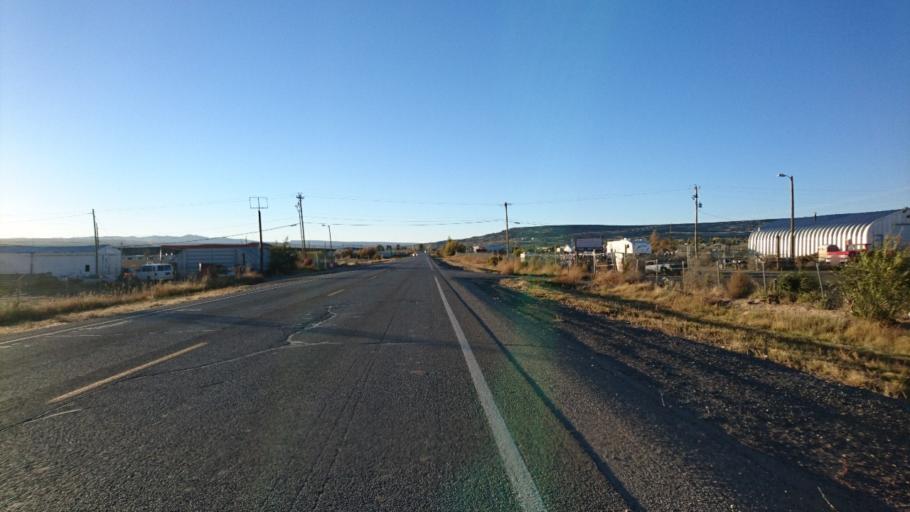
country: US
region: New Mexico
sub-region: Cibola County
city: Grants
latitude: 35.1362
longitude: -107.8214
